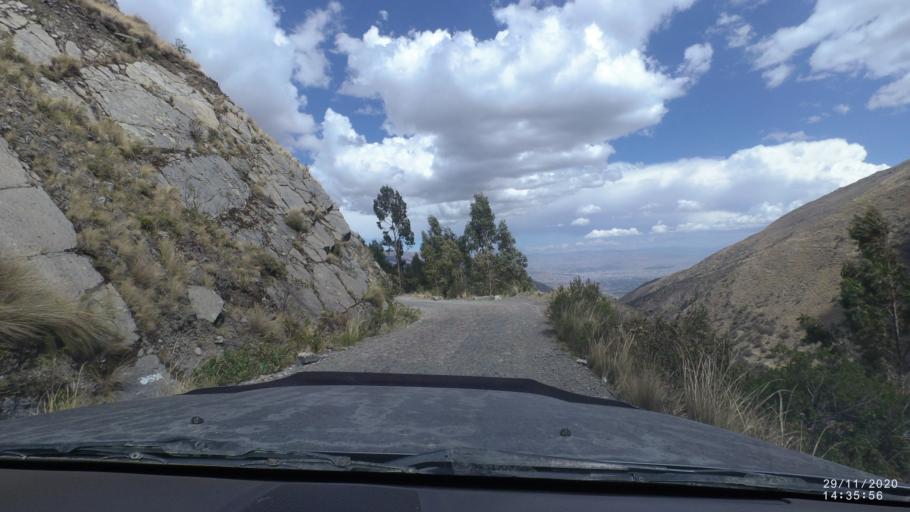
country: BO
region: Cochabamba
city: Sipe Sipe
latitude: -17.2719
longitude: -66.3331
